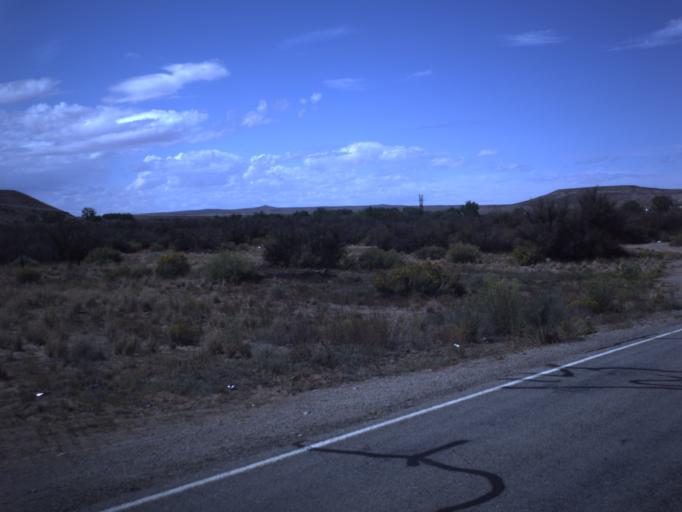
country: US
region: Utah
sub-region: San Juan County
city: Blanding
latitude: 37.2707
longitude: -109.3243
